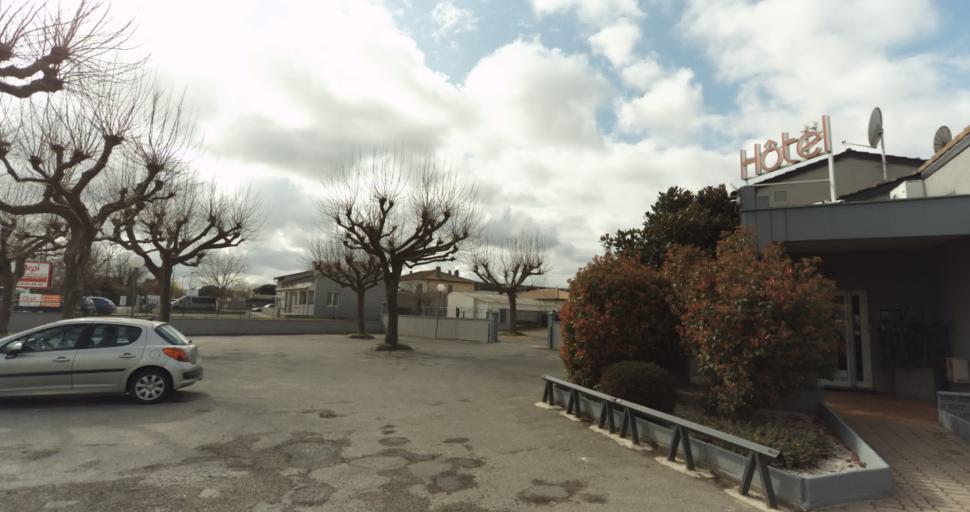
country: FR
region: Midi-Pyrenees
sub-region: Departement de la Haute-Garonne
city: Auterive
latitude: 43.3590
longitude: 1.4650
